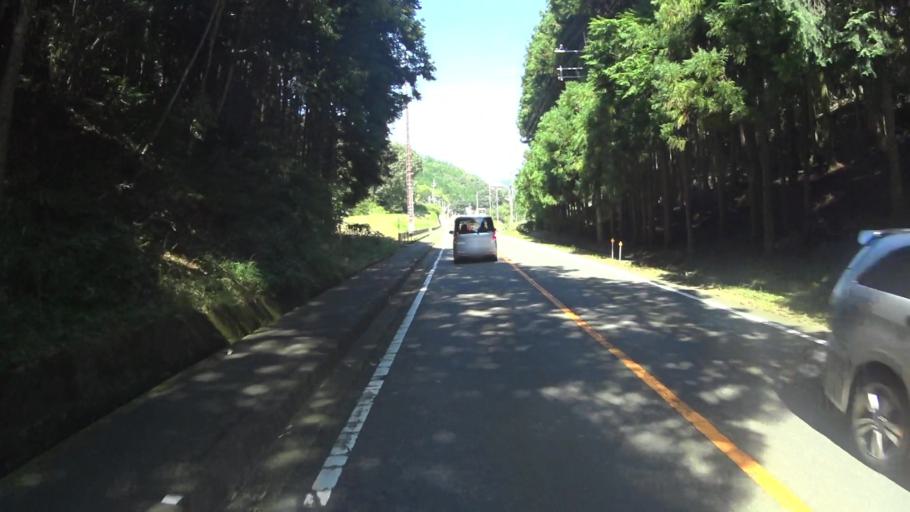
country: JP
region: Kyoto
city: Kameoka
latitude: 34.9628
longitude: 135.5115
